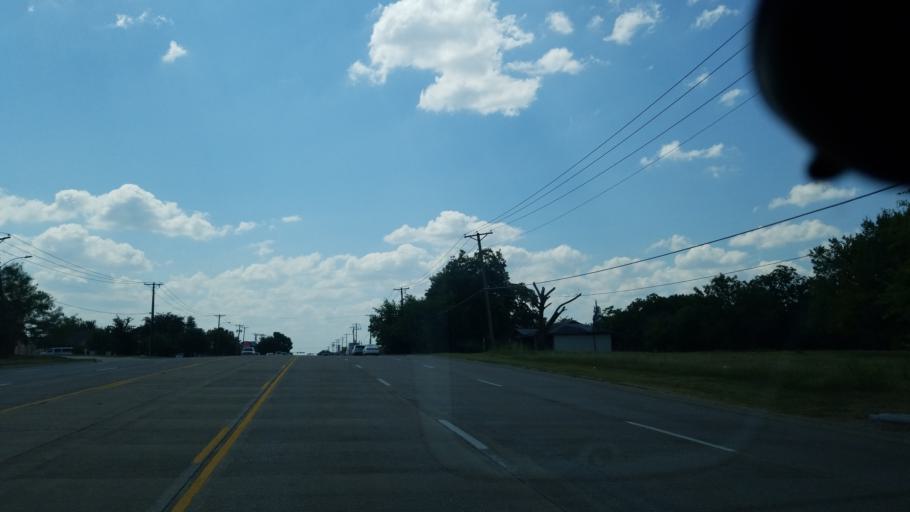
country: US
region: Texas
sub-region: Dallas County
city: Grand Prairie
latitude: 32.7143
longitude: -96.9942
